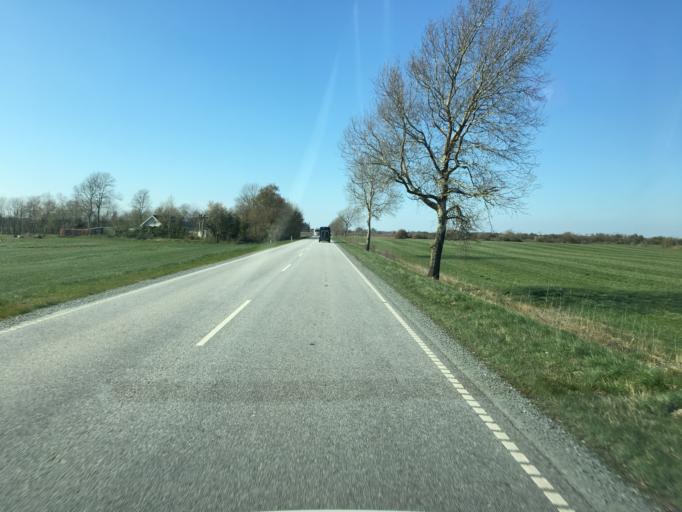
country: DK
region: South Denmark
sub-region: Aabenraa Kommune
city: Tinglev
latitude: 54.9581
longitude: 9.3327
